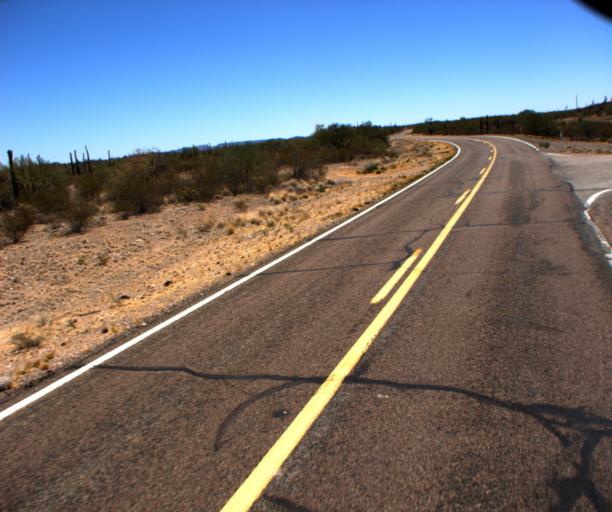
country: US
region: Arizona
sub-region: Pima County
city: Ajo
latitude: 32.2223
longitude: -112.6876
